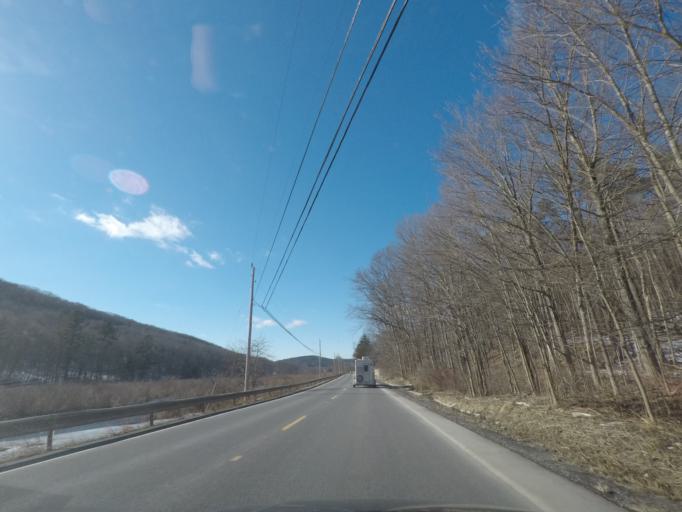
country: US
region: Massachusetts
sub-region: Berkshire County
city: Richmond
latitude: 42.4137
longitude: -73.4503
